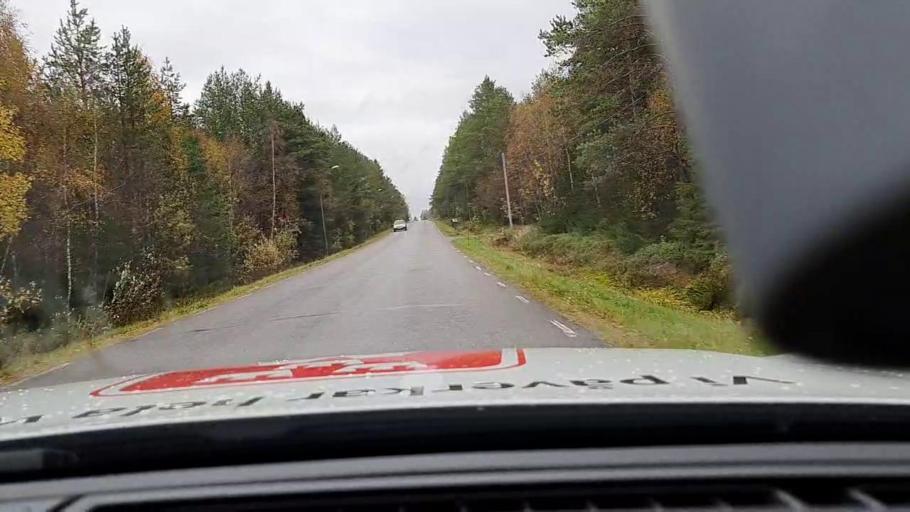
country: SE
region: Norrbotten
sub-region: Haparanda Kommun
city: Haparanda
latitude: 65.7870
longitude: 23.9210
